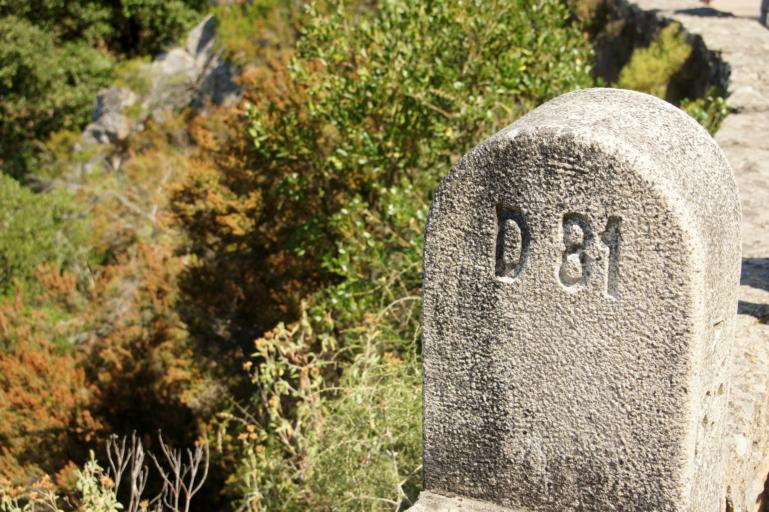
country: FR
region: Corsica
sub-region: Departement de la Corse-du-Sud
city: Cargese
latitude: 42.2478
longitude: 8.6548
